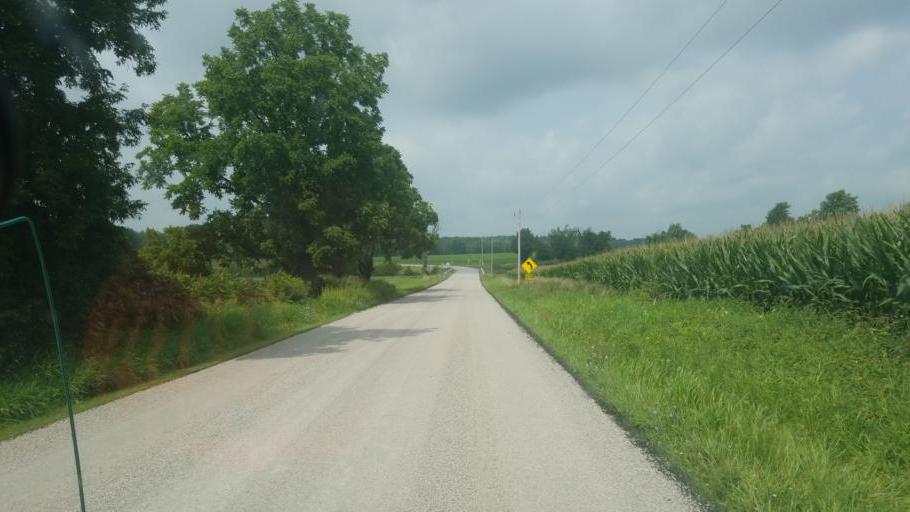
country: US
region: Ohio
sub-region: Huron County
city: Greenwich
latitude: 41.0644
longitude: -82.5321
